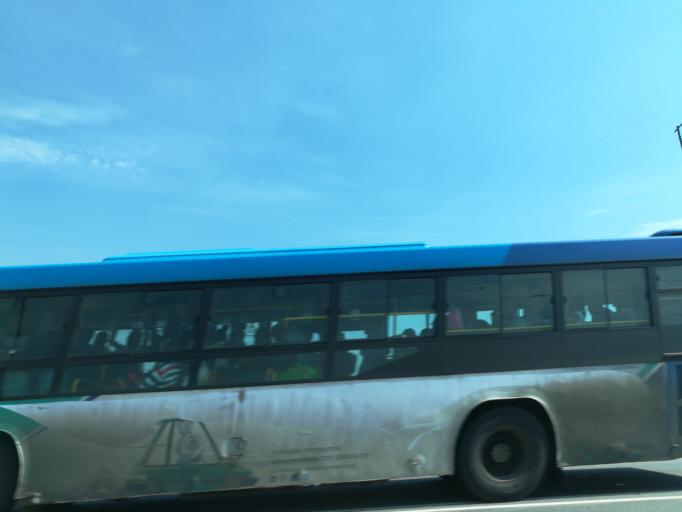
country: NG
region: Lagos
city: Ebute Ikorodu
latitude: 6.6088
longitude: 3.4375
